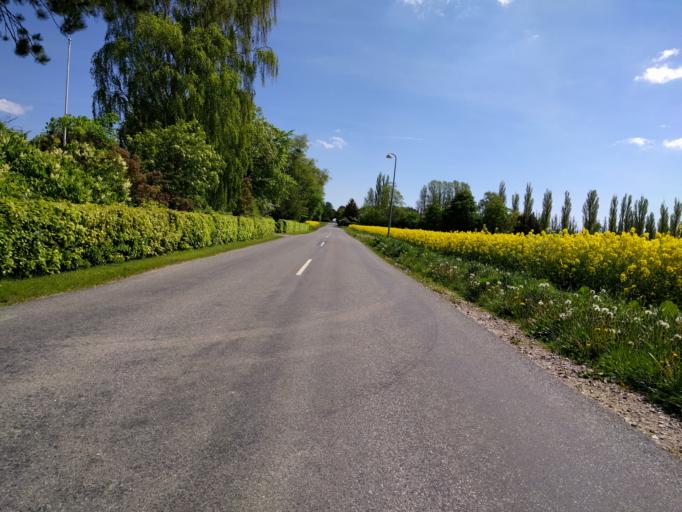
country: DK
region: Zealand
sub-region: Guldborgsund Kommune
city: Nykobing Falster
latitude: 54.7404
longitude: 11.9977
